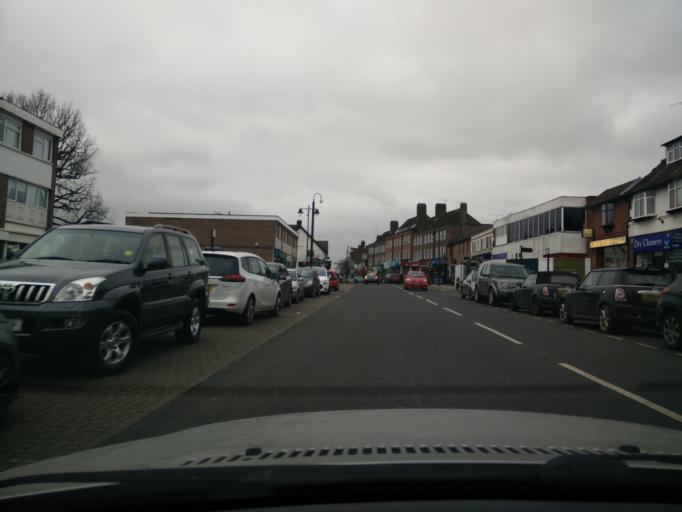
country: GB
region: England
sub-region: Buckinghamshire
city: Amersham on the Hill
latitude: 51.6786
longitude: -0.6052
